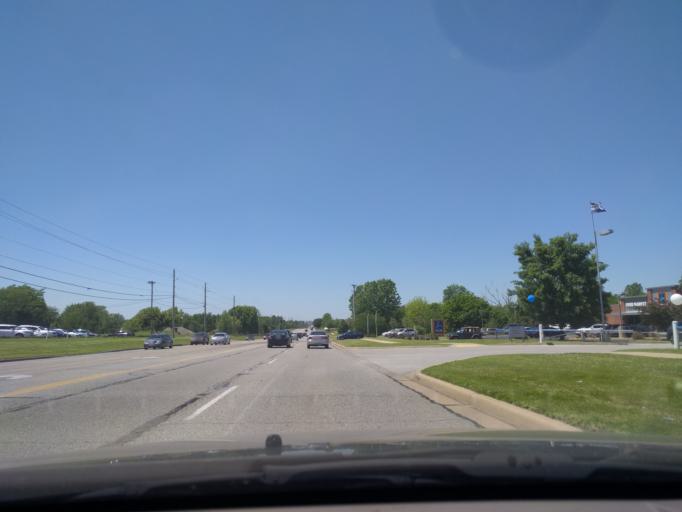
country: US
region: Oklahoma
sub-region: Tulsa County
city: Broken Arrow
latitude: 36.0610
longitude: -95.8196
